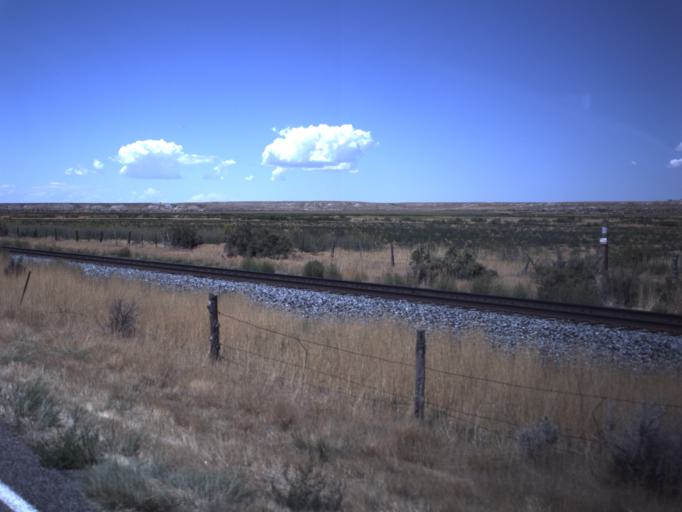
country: US
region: Utah
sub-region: Millard County
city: Delta
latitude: 39.5333
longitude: -112.3172
